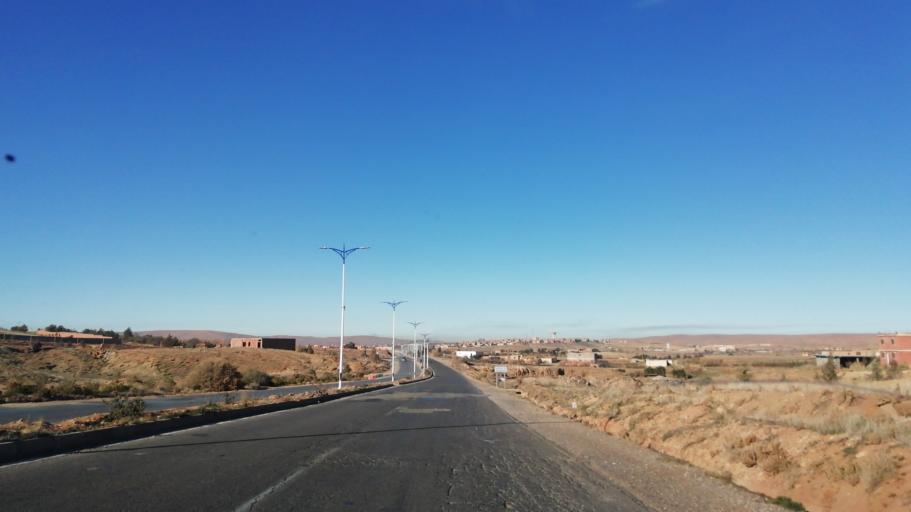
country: DZ
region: El Bayadh
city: El Bayadh
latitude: 33.6876
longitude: 1.0537
